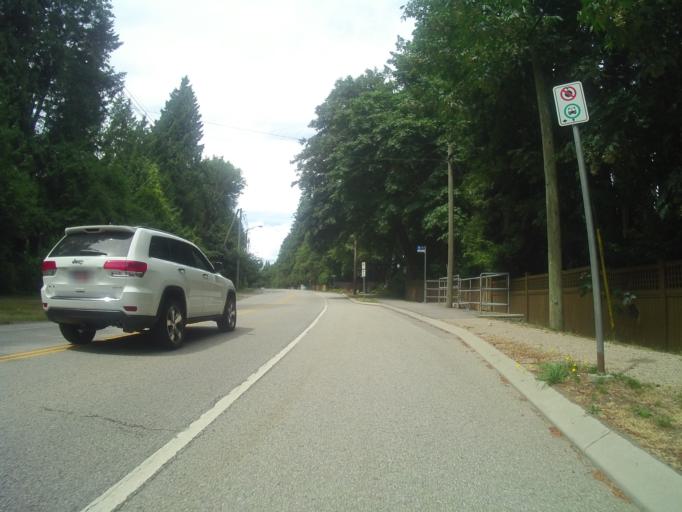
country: CA
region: British Columbia
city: Surrey
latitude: 49.0673
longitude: -122.8288
